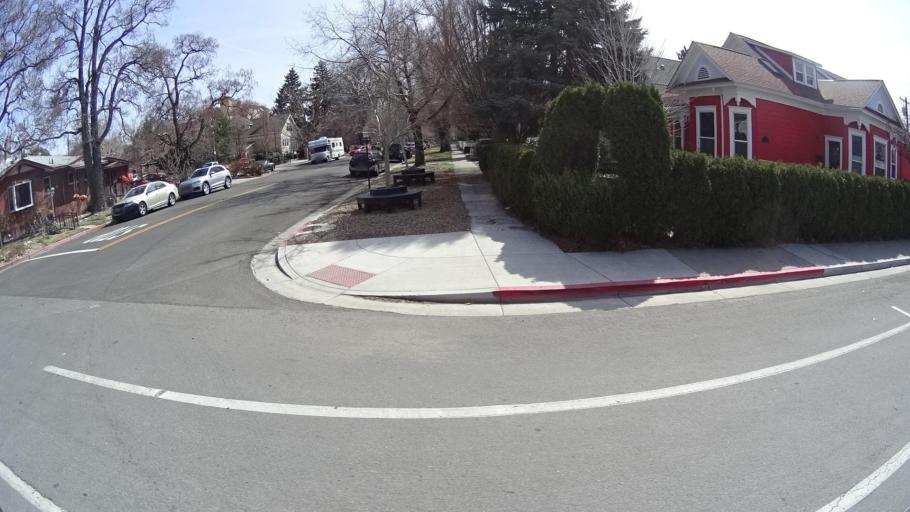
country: US
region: Nevada
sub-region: Washoe County
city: Reno
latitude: 39.5241
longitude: -119.8210
